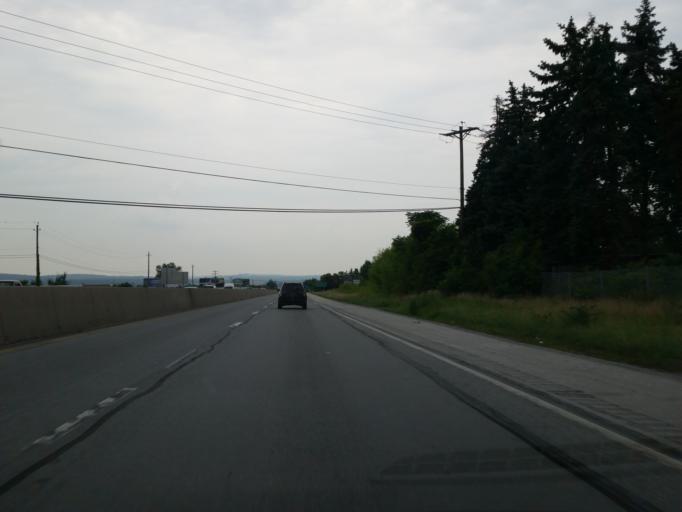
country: US
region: Pennsylvania
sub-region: York County
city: Emigsville
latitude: 40.0273
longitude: -76.7446
